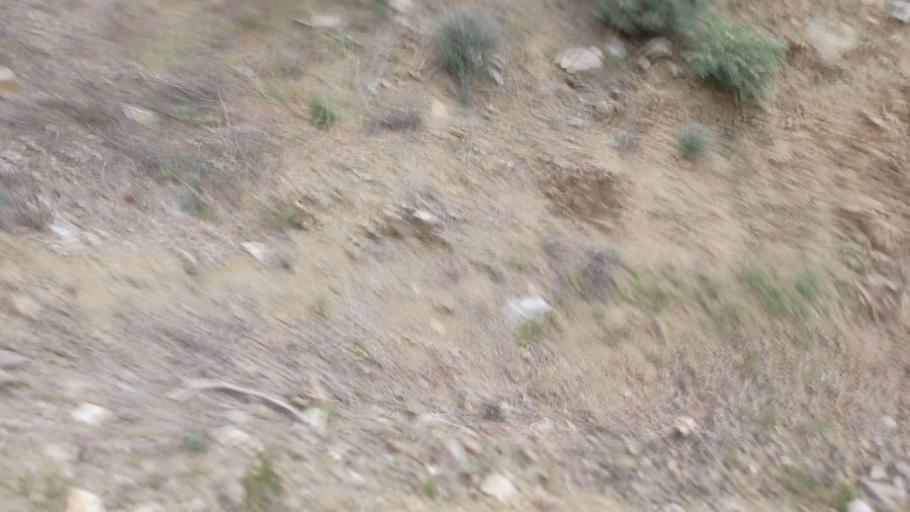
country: CY
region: Limassol
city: Parekklisha
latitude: 34.8613
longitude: 33.1021
